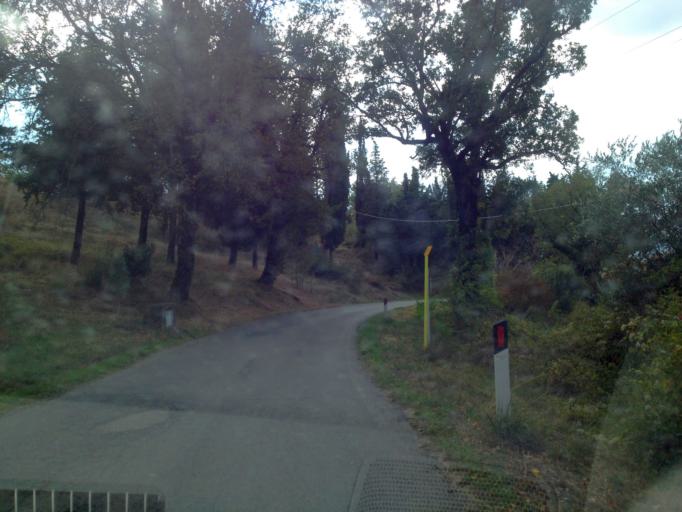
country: IT
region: Tuscany
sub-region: Province of Florence
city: Montebonello
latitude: 43.8582
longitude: 11.5078
